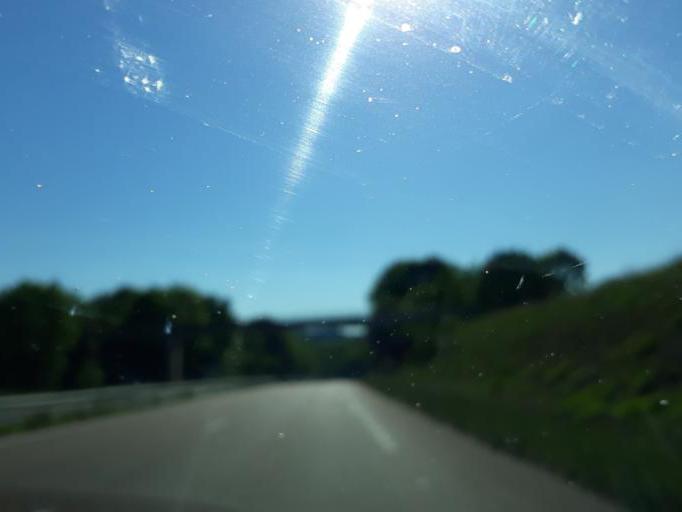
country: FR
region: Bourgogne
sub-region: Departement de la Cote-d'Or
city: Pouilly-en-Auxois
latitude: 47.2737
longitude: 4.6021
